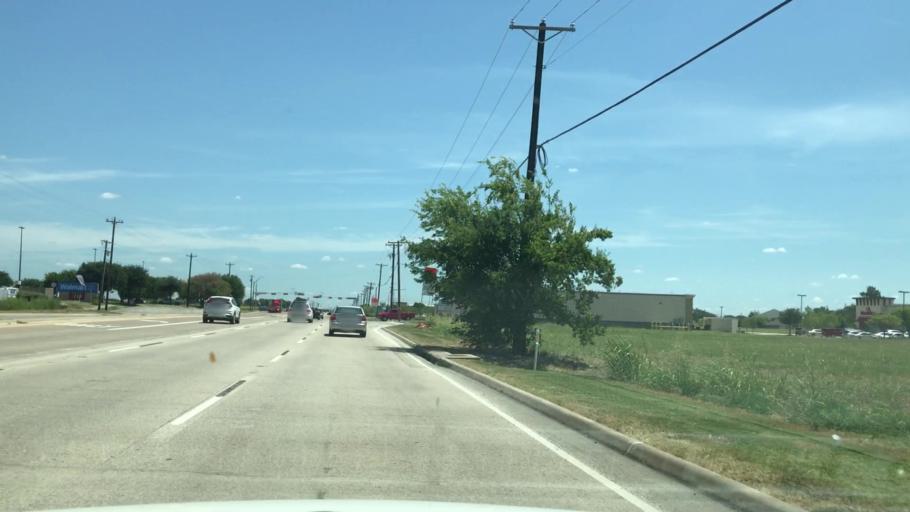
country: US
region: Texas
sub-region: Collin County
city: Wylie
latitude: 33.0228
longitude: -96.5133
